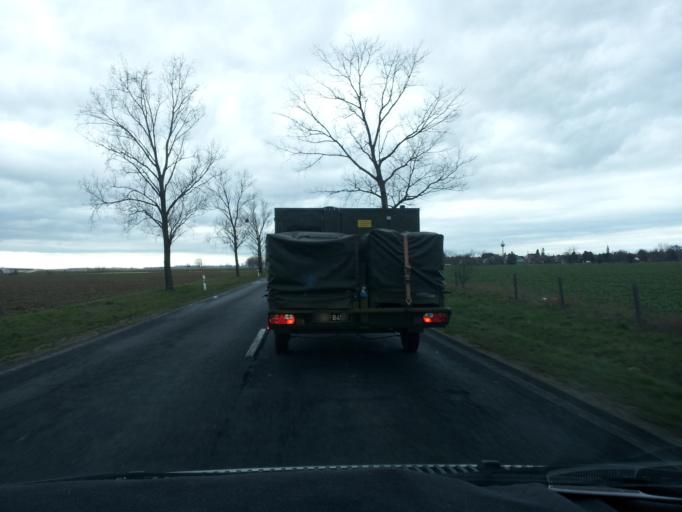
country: HU
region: Gyor-Moson-Sopron
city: Beled
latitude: 47.4680
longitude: 17.1195
